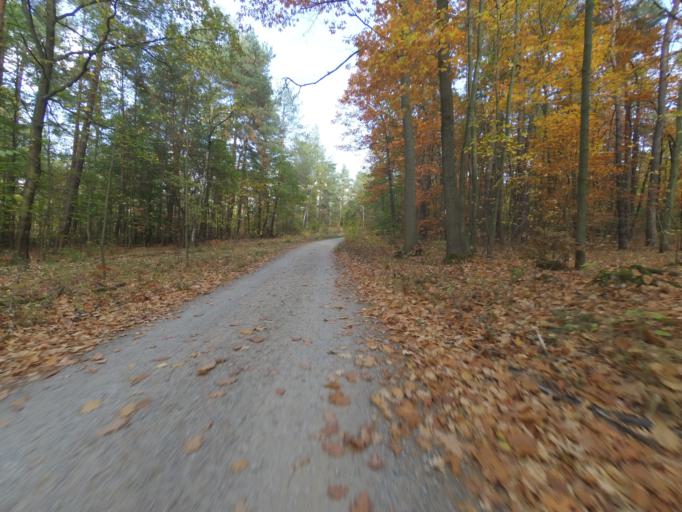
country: DE
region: Saxony
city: Albertstadt
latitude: 51.0910
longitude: 13.7899
